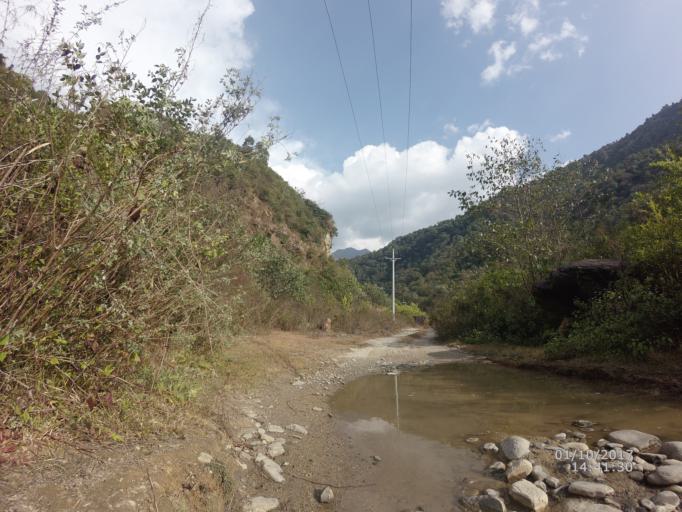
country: NP
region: Western Region
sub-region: Gandaki Zone
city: Pokhara
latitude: 28.3453
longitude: 83.9745
